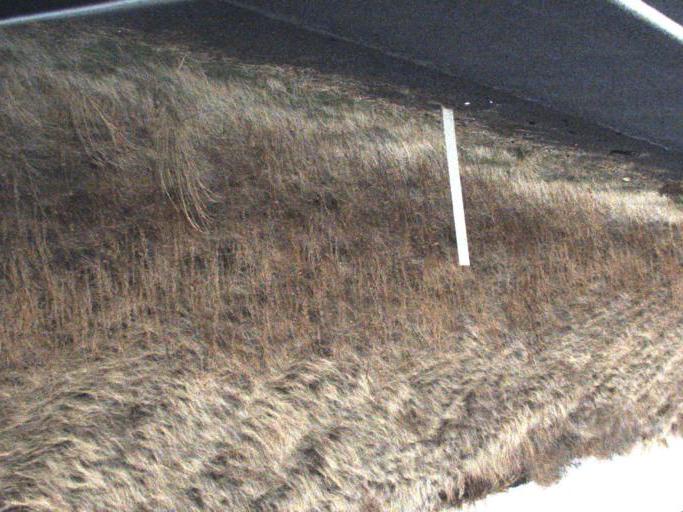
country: US
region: Washington
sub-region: Walla Walla County
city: Waitsburg
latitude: 46.1760
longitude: -118.1373
